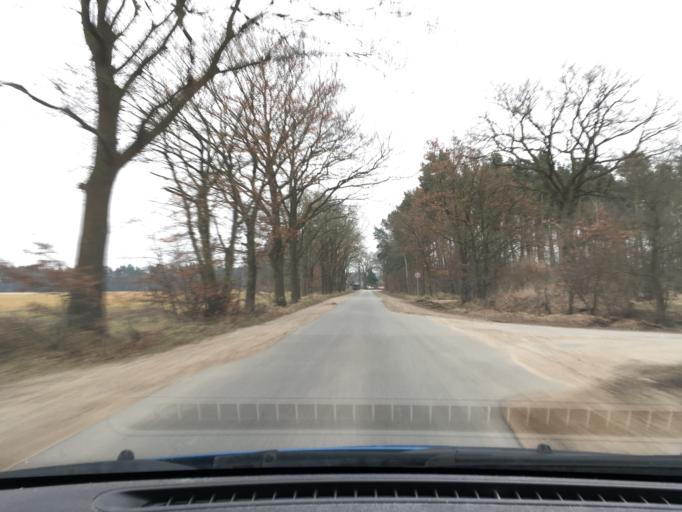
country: DE
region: Lower Saxony
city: Vogelsen
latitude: 53.2903
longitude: 10.3412
